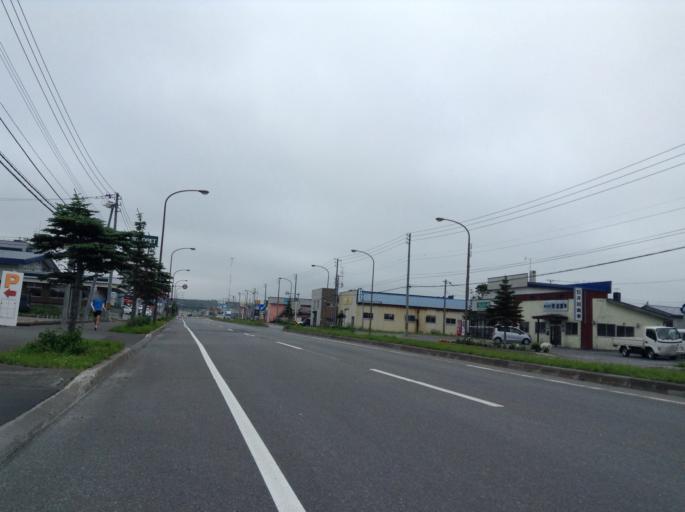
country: JP
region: Hokkaido
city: Wakkanai
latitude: 45.3853
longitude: 141.7069
